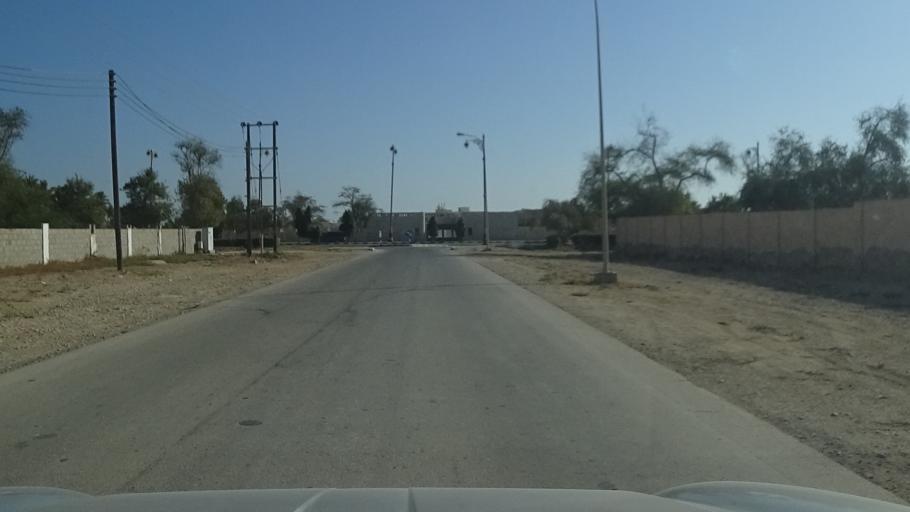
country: OM
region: Zufar
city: Salalah
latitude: 17.0272
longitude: 54.1666
